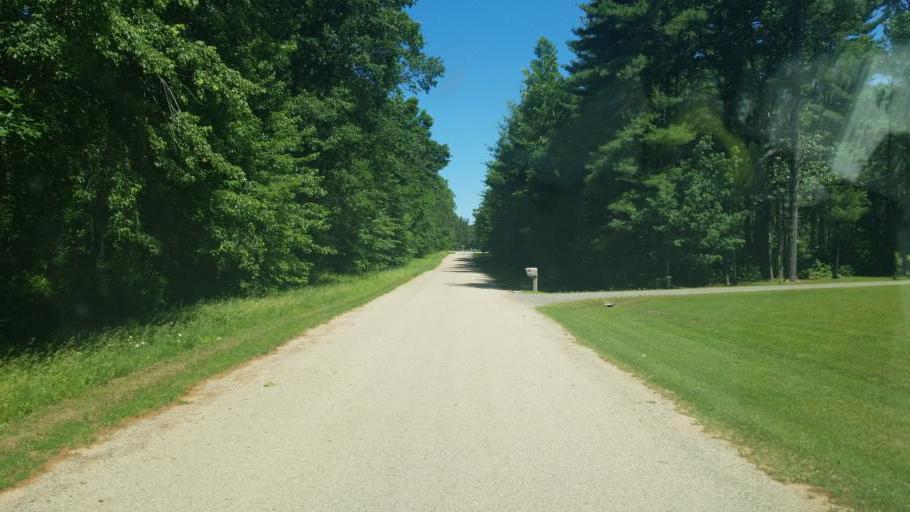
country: US
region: Wisconsin
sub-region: Juneau County
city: Mauston
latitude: 43.8739
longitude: -89.9485
